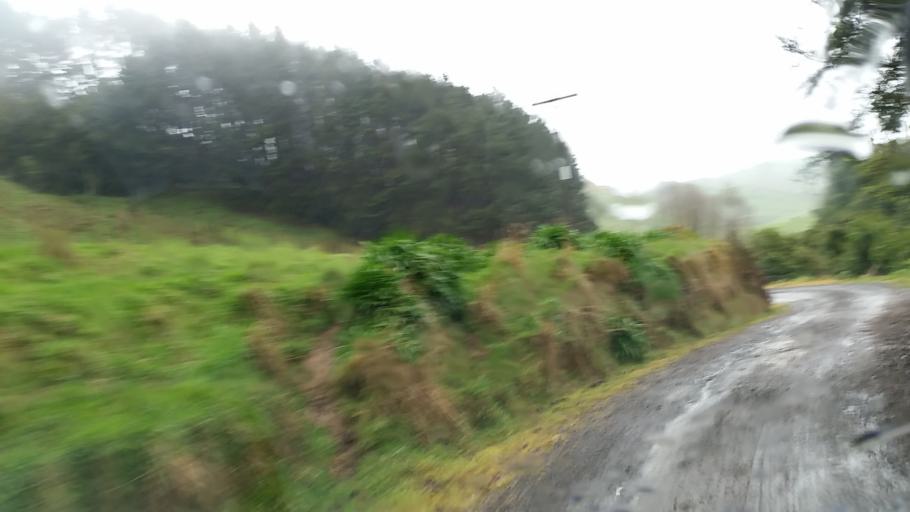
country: NZ
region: Taranaki
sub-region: South Taranaki District
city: Eltham
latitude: -39.4701
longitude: 174.4199
